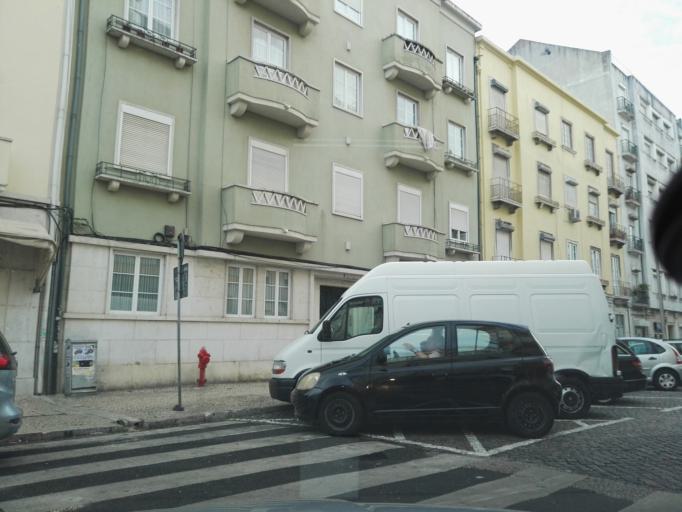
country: PT
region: Lisbon
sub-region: Lisbon
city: Lisbon
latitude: 38.7337
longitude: -9.1315
